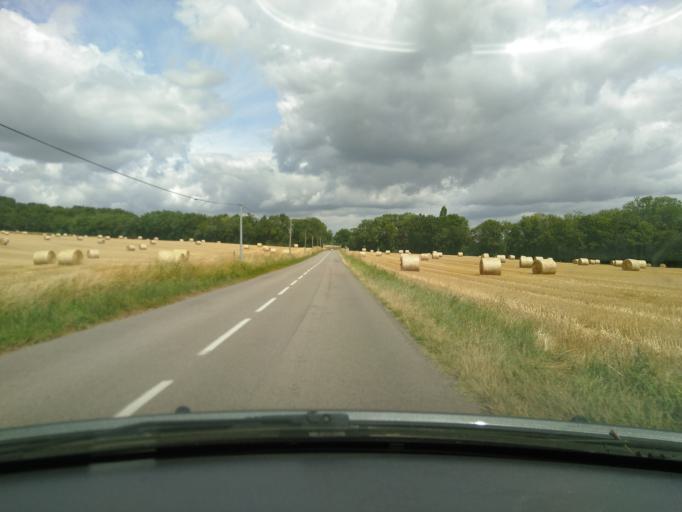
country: FR
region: Rhone-Alpes
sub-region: Departement de l'Isere
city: Beaurepaire
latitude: 45.3926
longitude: 5.0390
